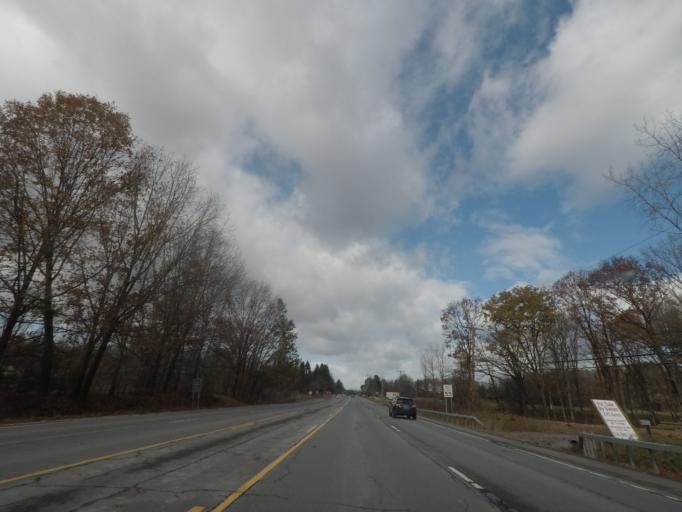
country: US
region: New York
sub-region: Saratoga County
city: Ballston Spa
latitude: 42.9868
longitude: -73.7873
